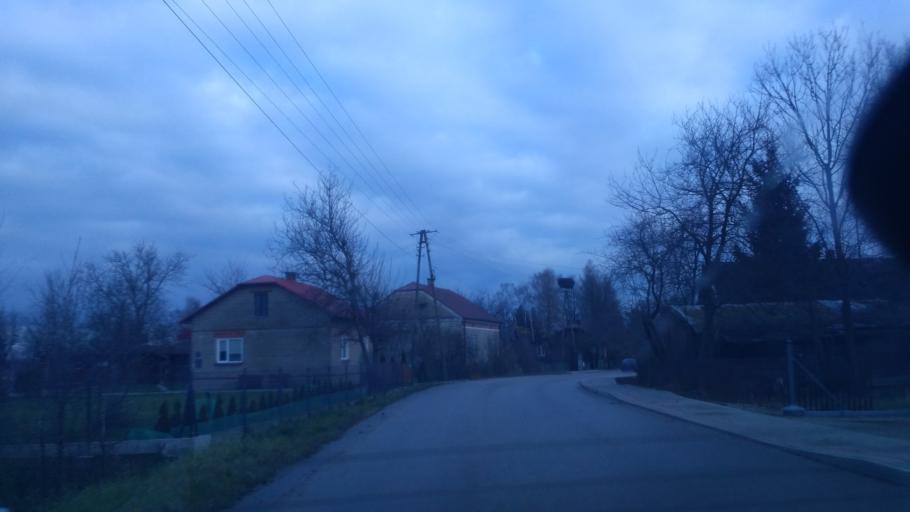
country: PL
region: Subcarpathian Voivodeship
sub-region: Powiat lancucki
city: Czarna
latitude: 50.1014
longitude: 22.1476
